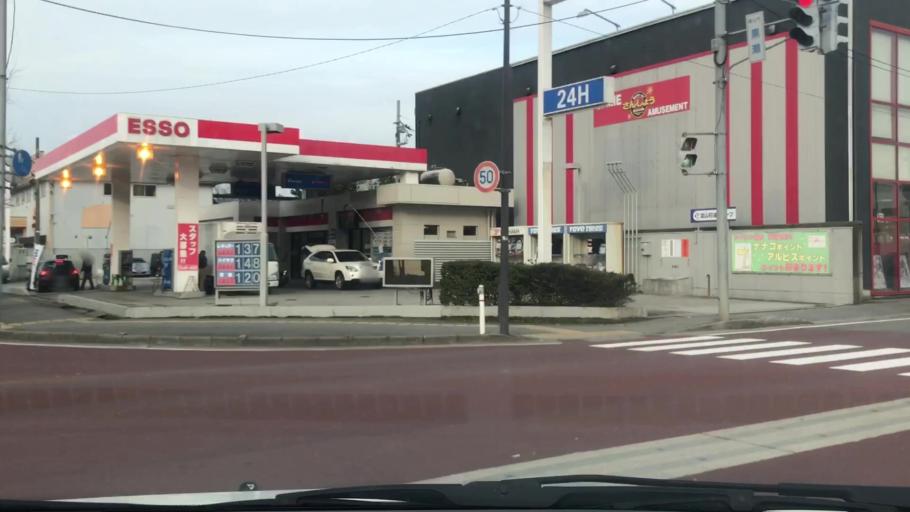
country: JP
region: Toyama
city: Toyama-shi
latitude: 36.6669
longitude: 137.2016
